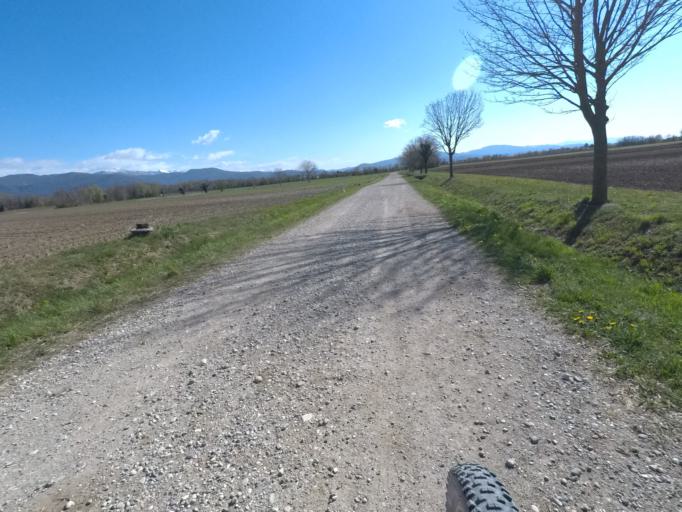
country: IT
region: Friuli Venezia Giulia
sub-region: Provincia di Udine
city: Moimacco
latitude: 46.0907
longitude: 13.3546
